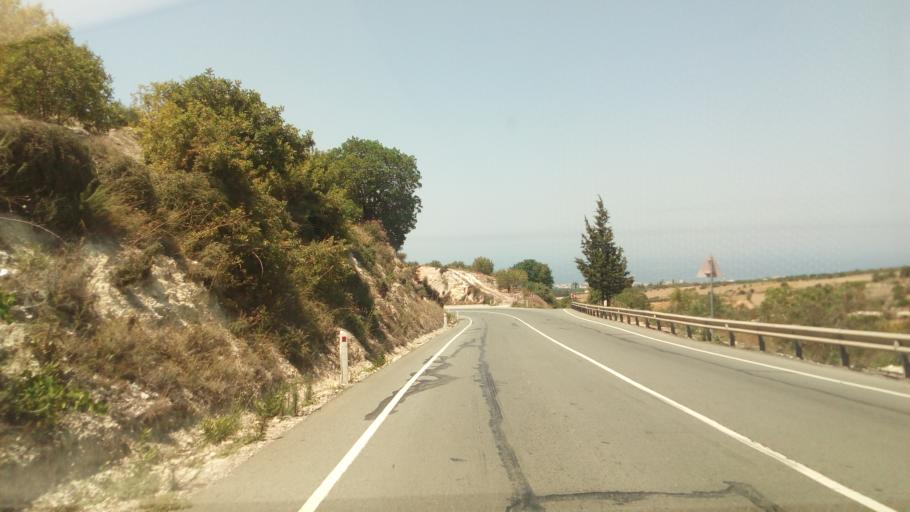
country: CY
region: Pafos
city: Mesogi
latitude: 34.8309
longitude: 32.4658
